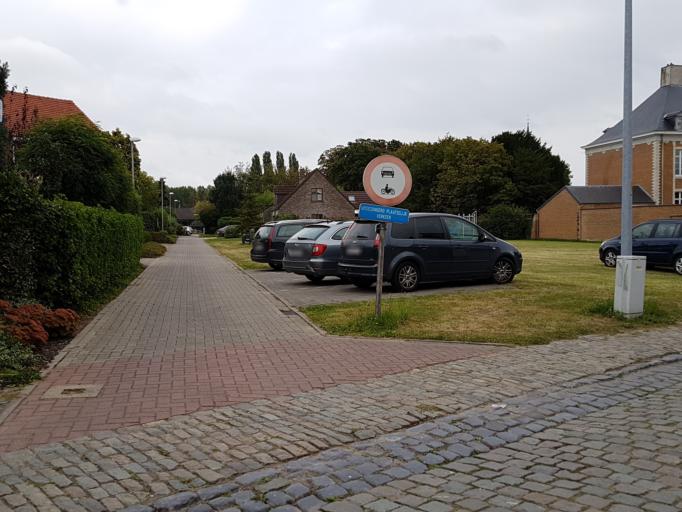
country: BE
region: Flanders
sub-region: Provincie Vlaams-Brabant
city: Rotselaar
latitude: 50.9564
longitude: 4.6752
